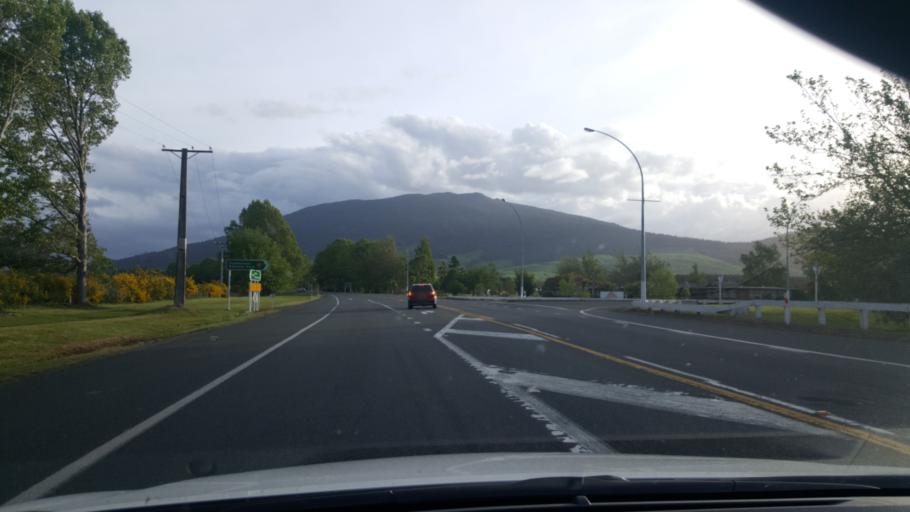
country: NZ
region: Waikato
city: Turangi
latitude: -38.9957
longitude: 175.8055
